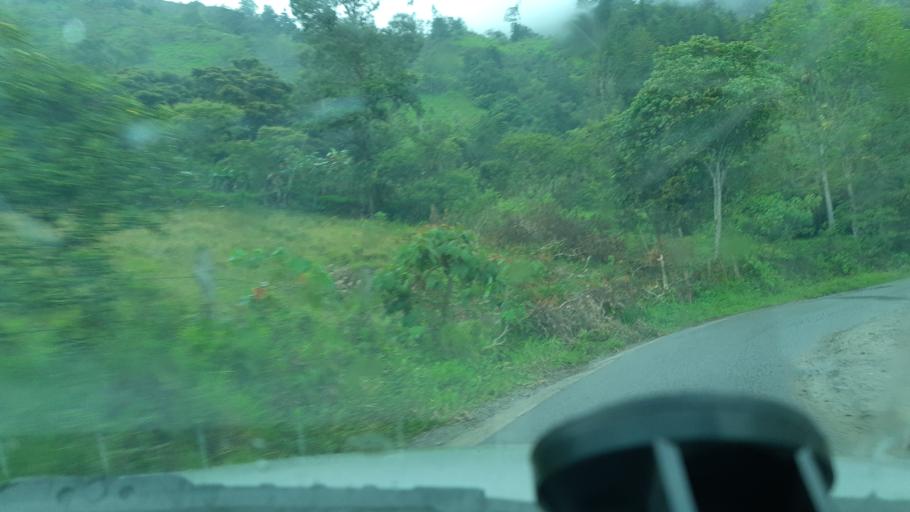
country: CO
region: Boyaca
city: Chinavita
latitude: 5.2068
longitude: -73.3899
